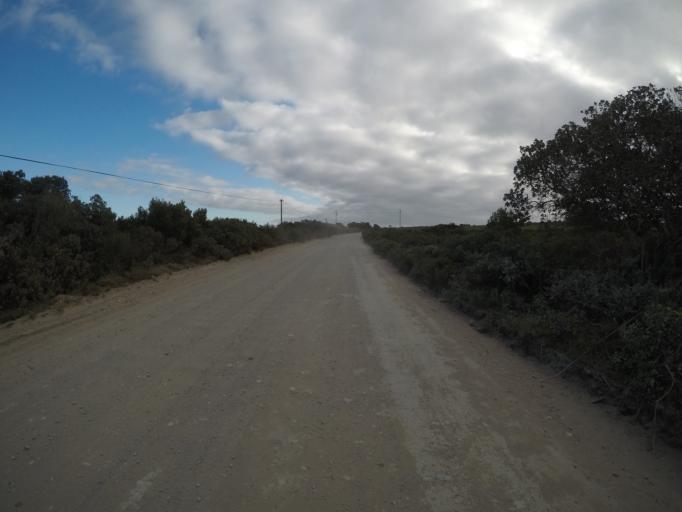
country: ZA
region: Western Cape
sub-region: Eden District Municipality
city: Riversdale
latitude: -34.4182
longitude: 21.3423
